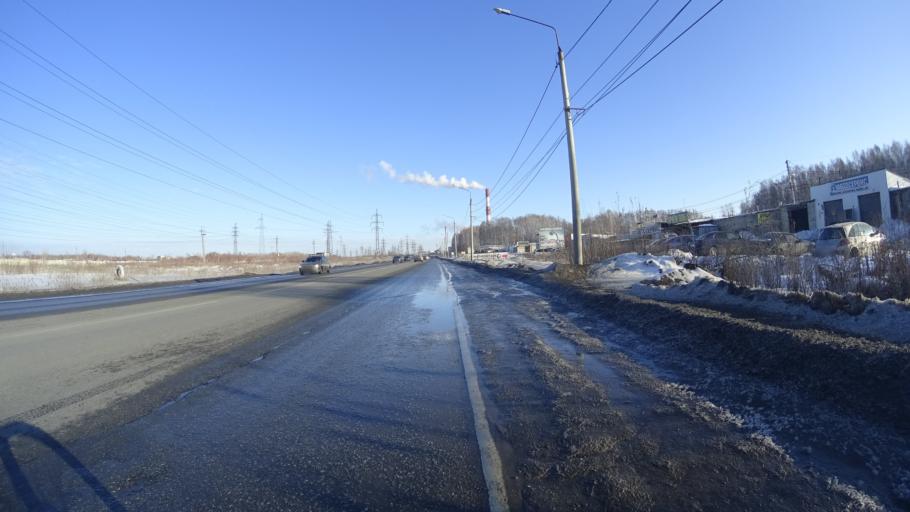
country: RU
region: Chelyabinsk
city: Roshchino
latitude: 55.2111
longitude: 61.3098
